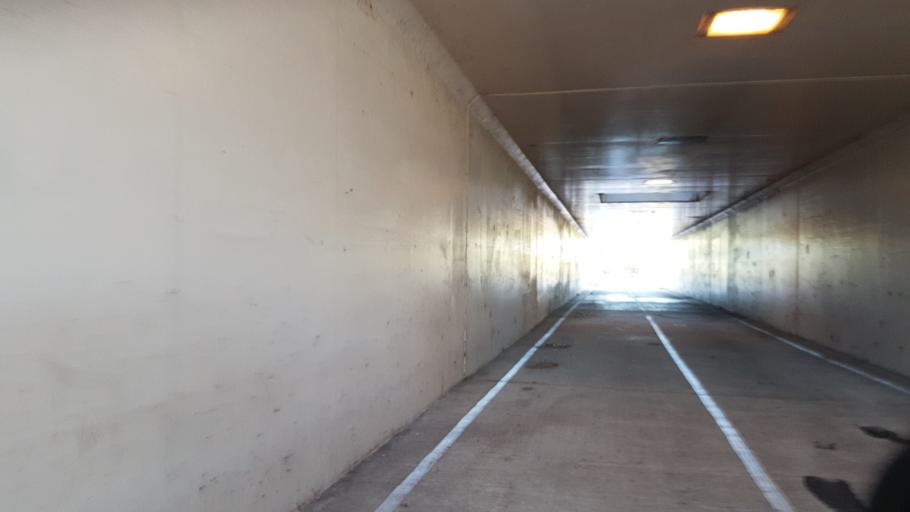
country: AU
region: Western Australia
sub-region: Kwinana
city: Bertram
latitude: -32.2316
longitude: 115.8490
